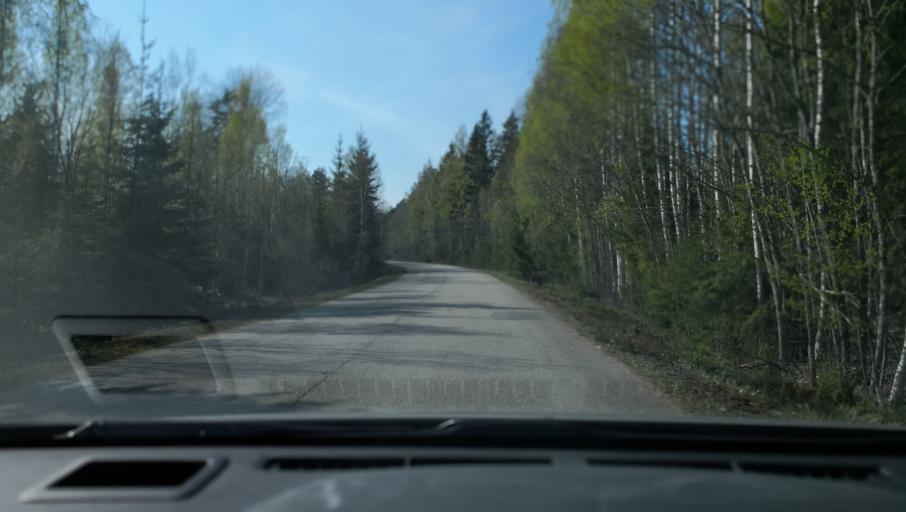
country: SE
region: Uppsala
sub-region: Heby Kommun
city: Tarnsjo
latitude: 60.2648
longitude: 16.9245
